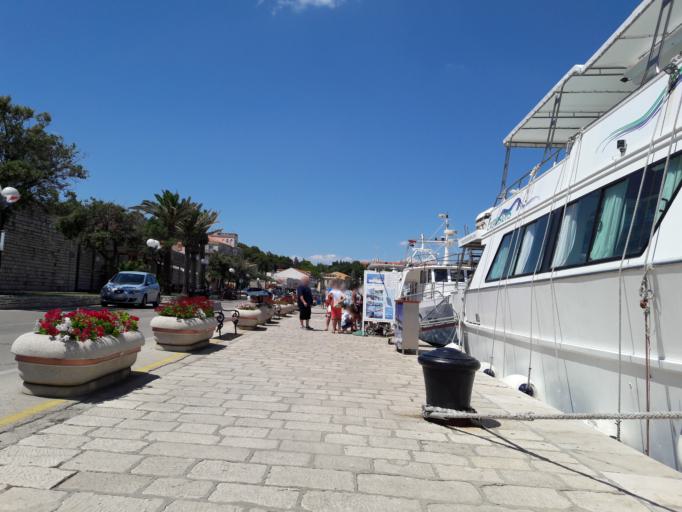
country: HR
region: Primorsko-Goranska
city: Banjol
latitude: 44.7572
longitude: 14.7614
